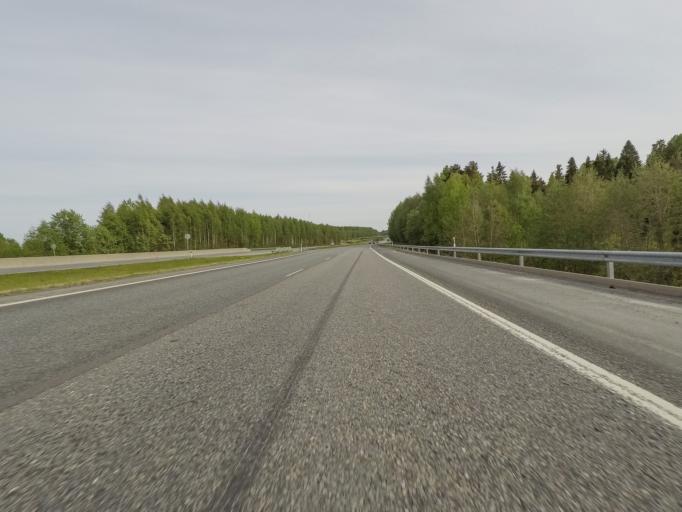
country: FI
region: Haeme
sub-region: Haemeenlinna
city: Parola
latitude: 61.0532
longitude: 24.3517
